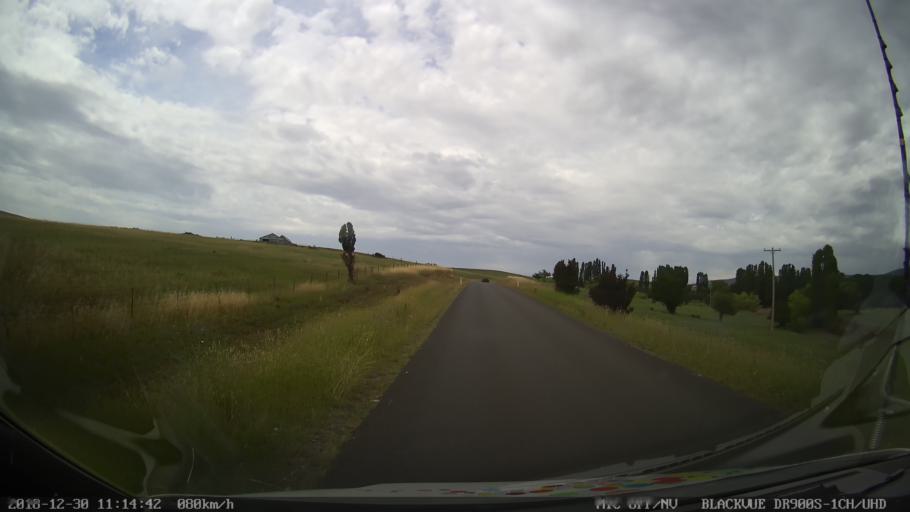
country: AU
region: New South Wales
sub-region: Snowy River
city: Jindabyne
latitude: -36.5385
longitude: 148.7283
